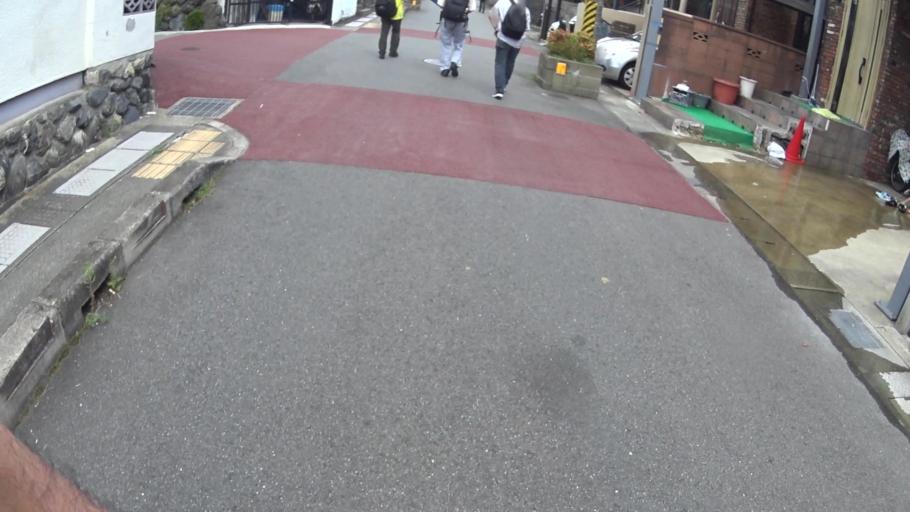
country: JP
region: Kyoto
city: Yawata
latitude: 34.9082
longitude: 135.6965
